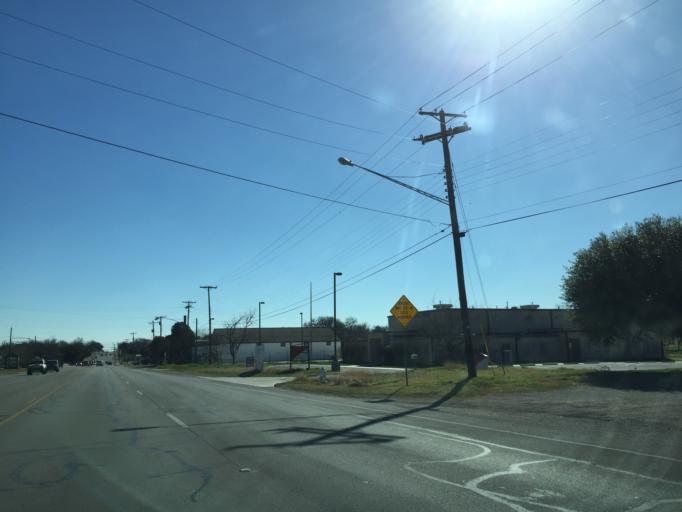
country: US
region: Texas
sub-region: Williamson County
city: Taylor
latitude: 30.5818
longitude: -97.4110
